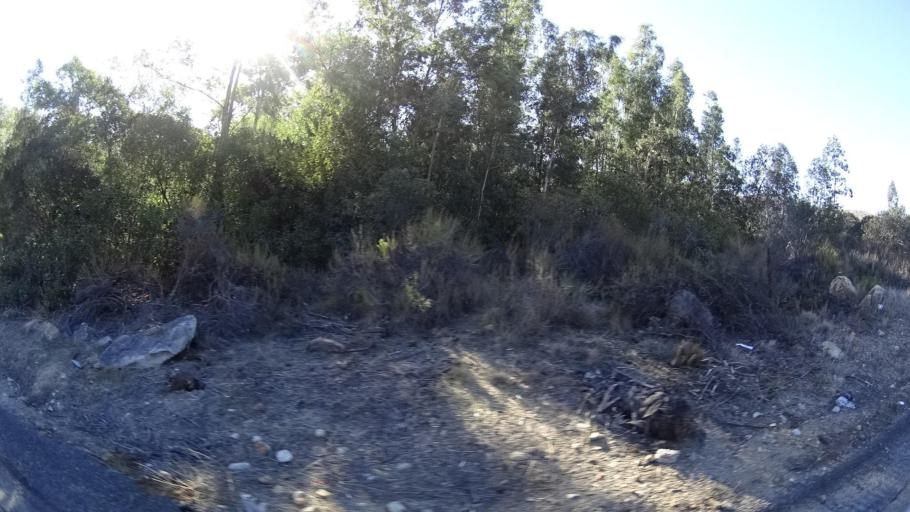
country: US
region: California
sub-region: San Diego County
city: Jamul
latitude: 32.6361
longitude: -116.8851
